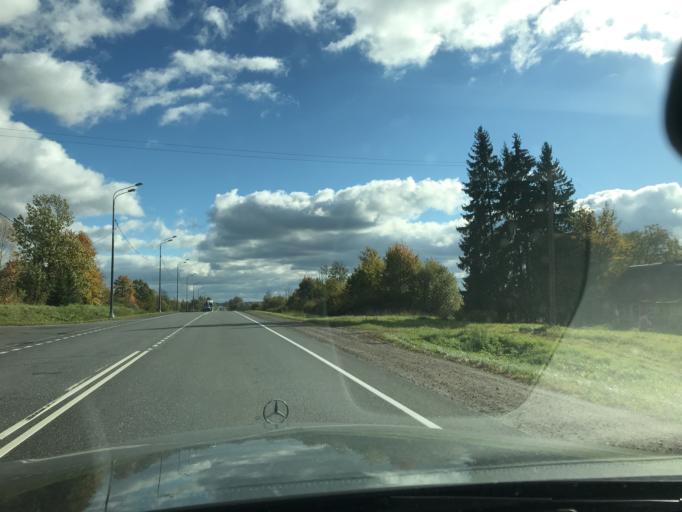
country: RU
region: Pskov
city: Ostrov
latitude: 57.1161
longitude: 28.5309
